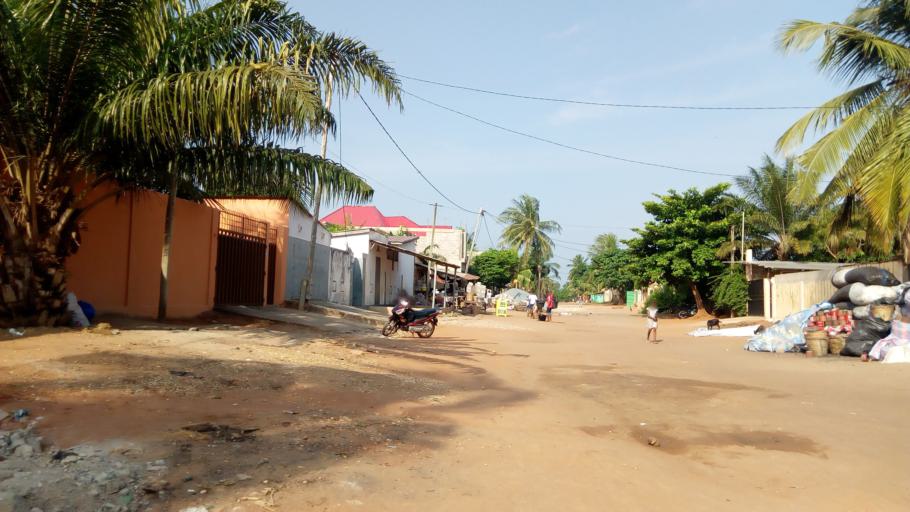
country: TG
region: Maritime
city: Lome
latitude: 6.1823
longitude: 1.1876
